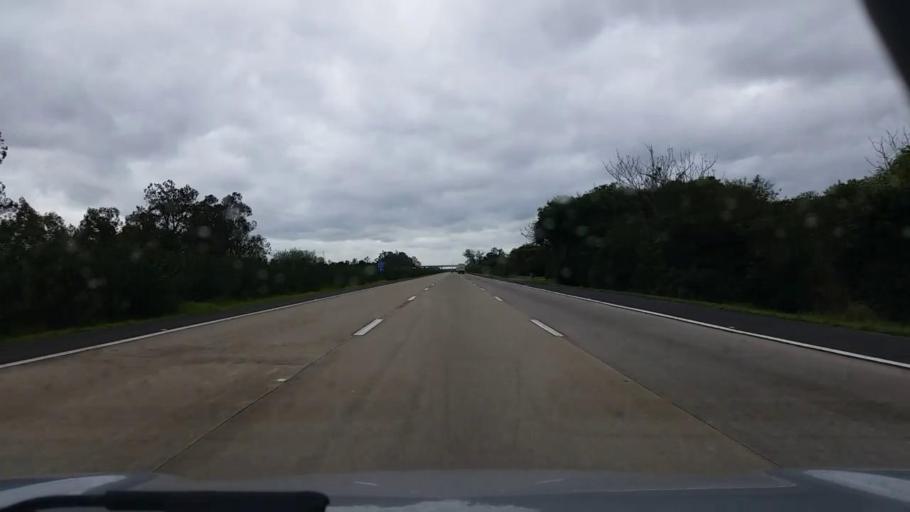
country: BR
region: Rio Grande do Sul
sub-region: Rolante
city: Rolante
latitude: -29.8863
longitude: -50.6469
